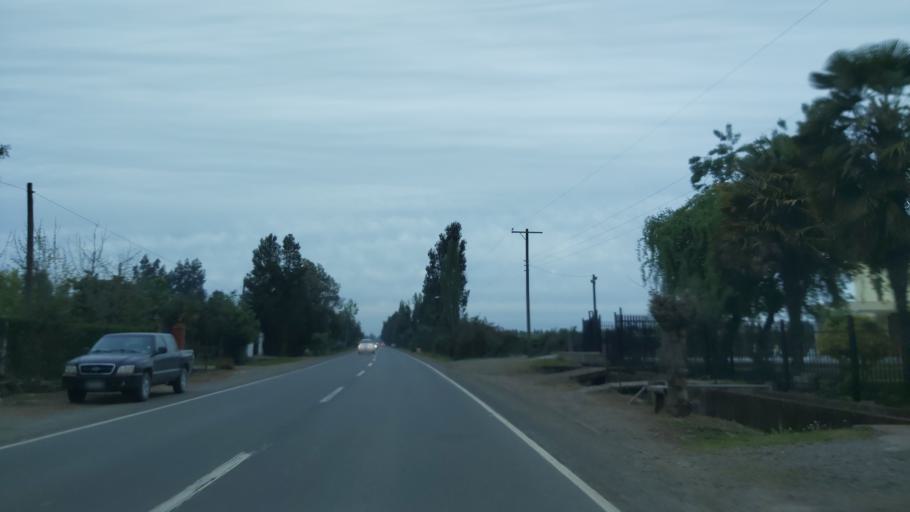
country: CL
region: Maule
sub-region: Provincia de Linares
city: Colbun
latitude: -35.7347
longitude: -71.4893
